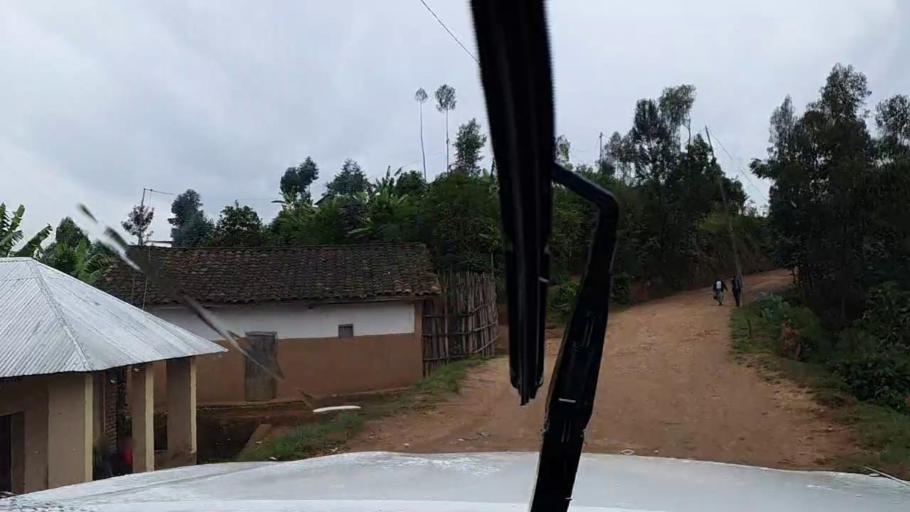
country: RW
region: Southern Province
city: Nzega
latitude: -2.4639
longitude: 29.4941
